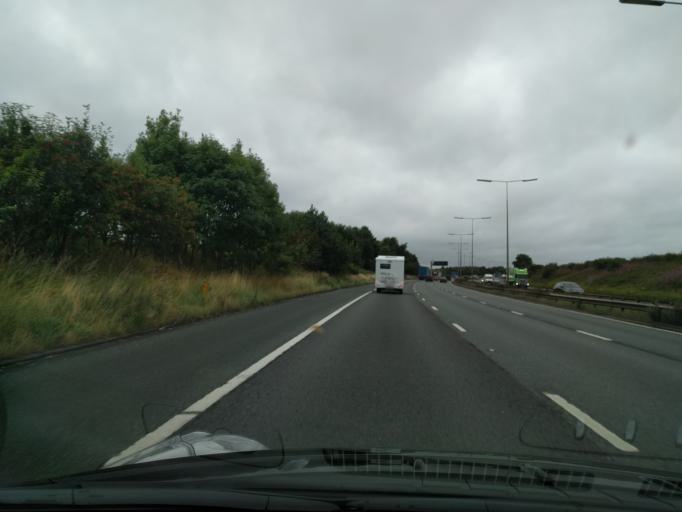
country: GB
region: England
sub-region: St. Helens
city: Newton-le-Willows
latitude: 53.4491
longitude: -2.5963
